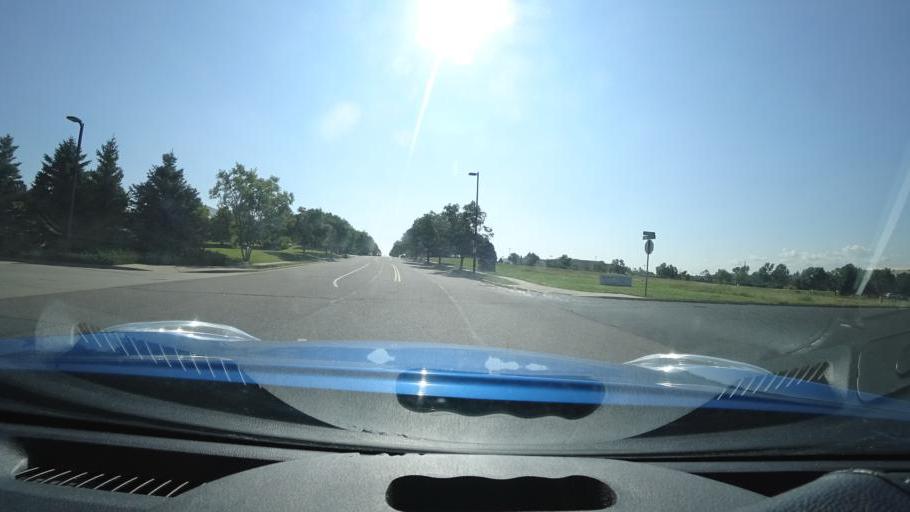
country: US
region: Colorado
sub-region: Adams County
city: Aurora
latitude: 39.7167
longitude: -104.7970
